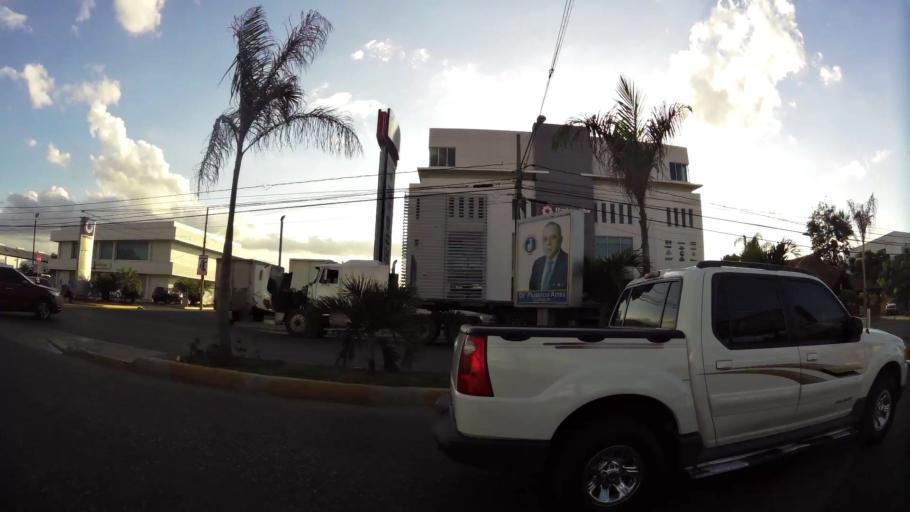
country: DO
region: Santiago
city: Santiago de los Caballeros
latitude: 19.4775
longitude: -70.7168
